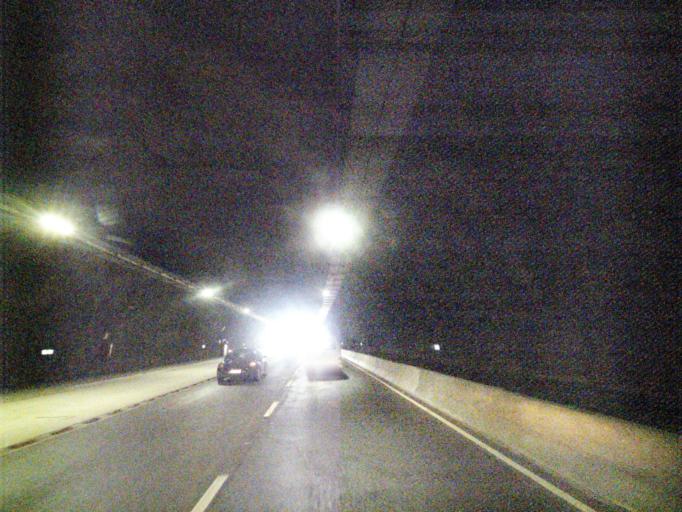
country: BR
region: Rio de Janeiro
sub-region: Niteroi
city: Niteroi
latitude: -22.9360
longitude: -43.0858
